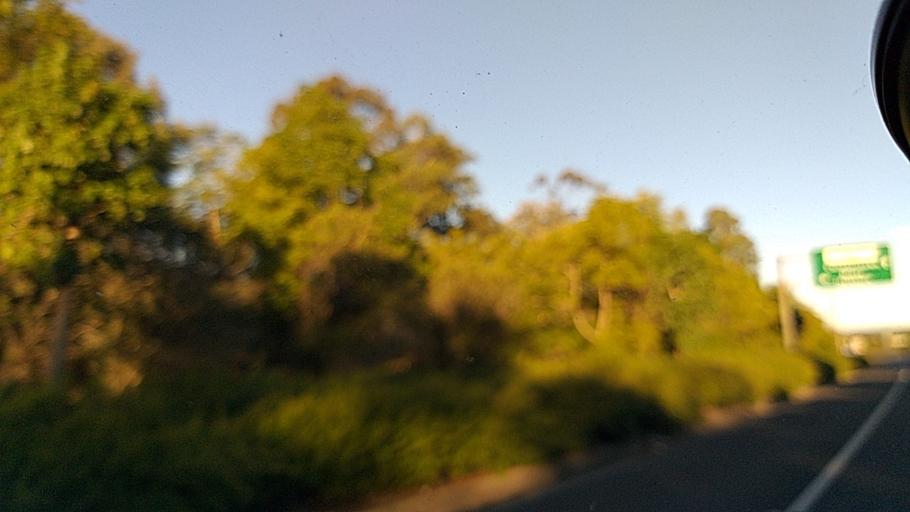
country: AU
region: New South Wales
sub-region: Campbelltown Municipality
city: Leumeah
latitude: -34.0355
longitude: 150.8251
